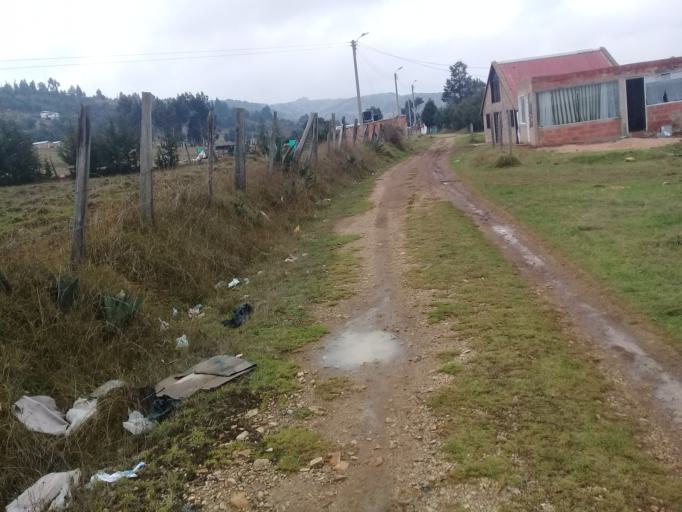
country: CO
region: Boyaca
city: Siachoque
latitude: 5.5610
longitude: -73.2795
